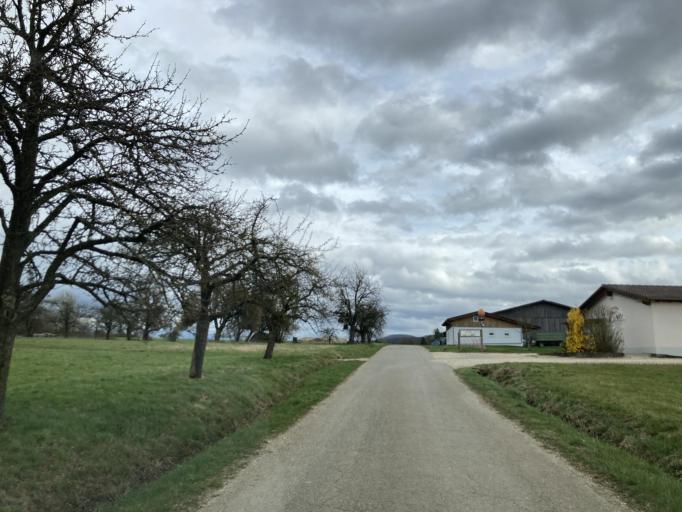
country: DE
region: Baden-Wuerttemberg
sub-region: Tuebingen Region
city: Gomaringen
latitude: 48.4812
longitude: 9.1161
